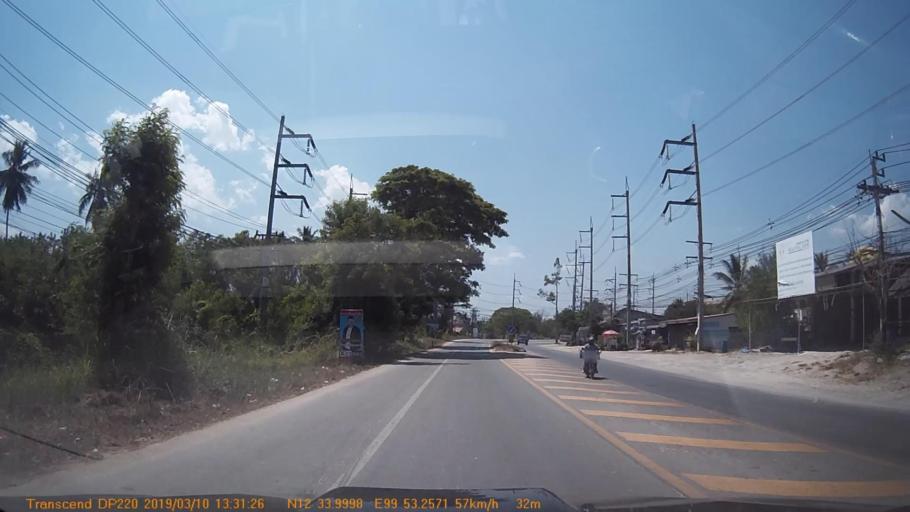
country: TH
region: Prachuap Khiri Khan
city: Hua Hin
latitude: 12.5666
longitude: 99.8873
